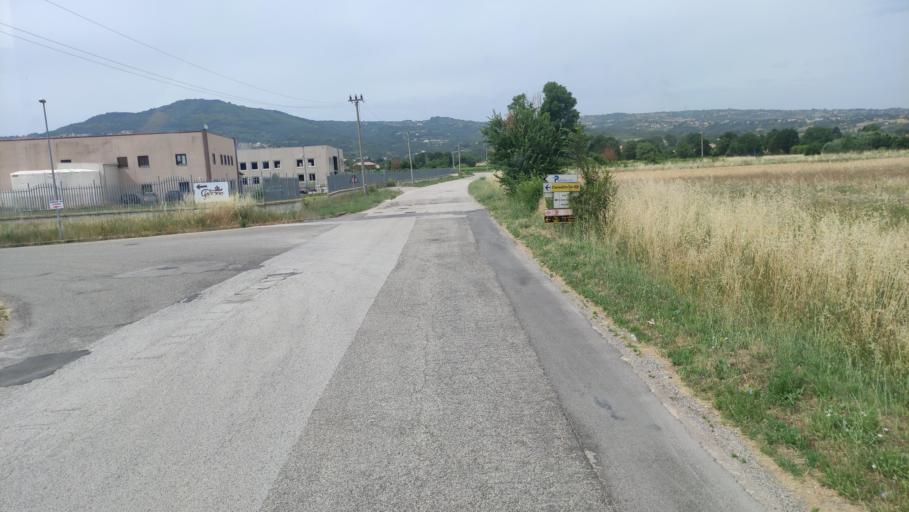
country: IT
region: Campania
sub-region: Provincia di Avellino
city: Sturno
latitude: 41.0517
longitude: 15.1212
